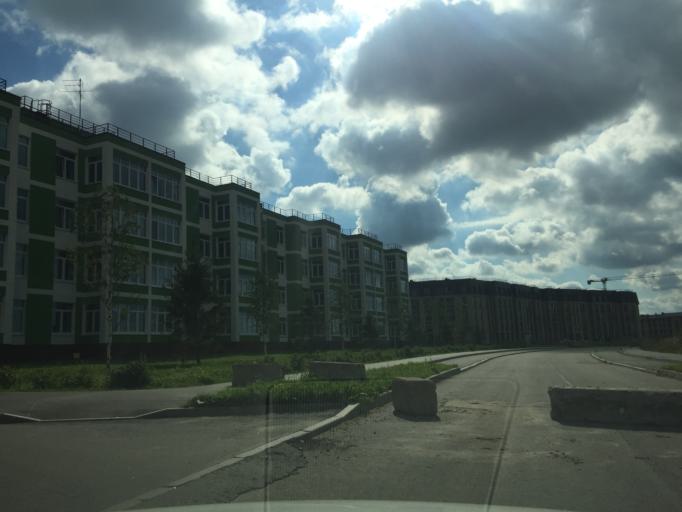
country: RU
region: St.-Petersburg
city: Aleksandrovskaya
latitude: 59.7536
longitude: 30.3673
